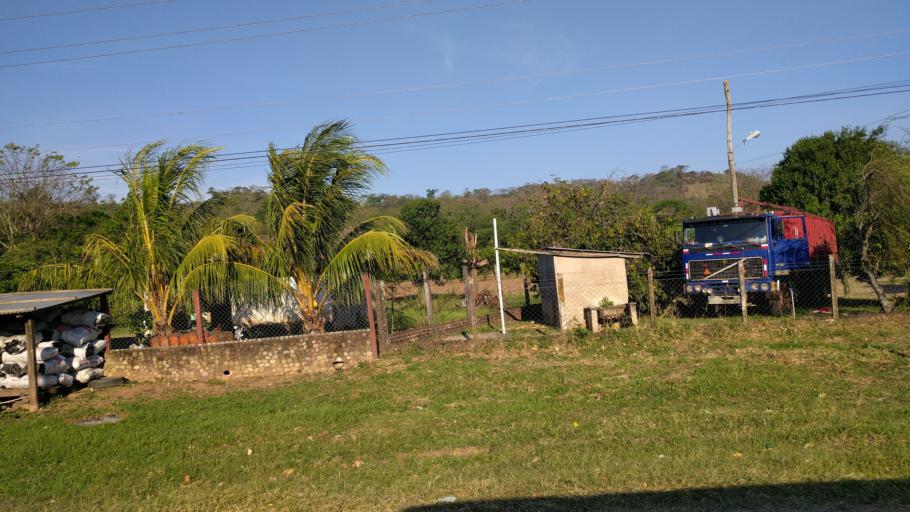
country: BO
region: Santa Cruz
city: Jorochito
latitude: -18.0953
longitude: -63.4503
